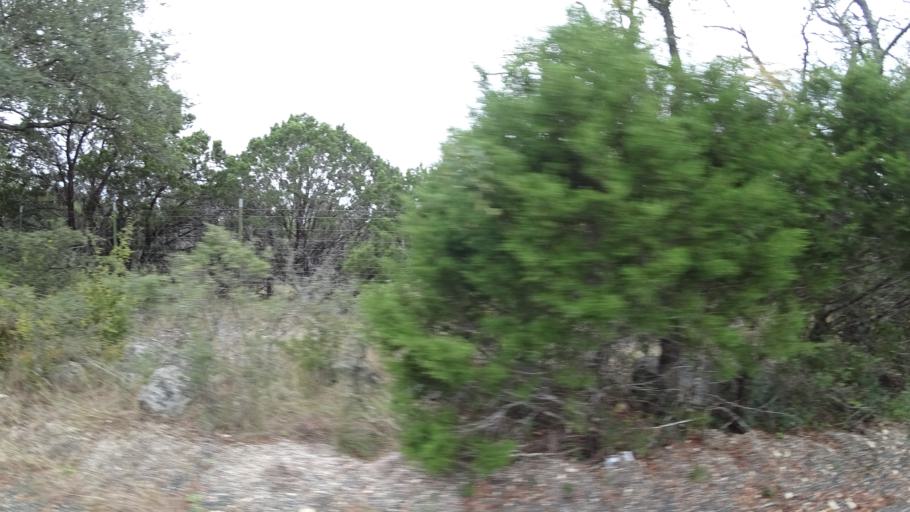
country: US
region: Texas
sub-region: Travis County
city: Lakeway
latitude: 30.3512
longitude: -97.9447
